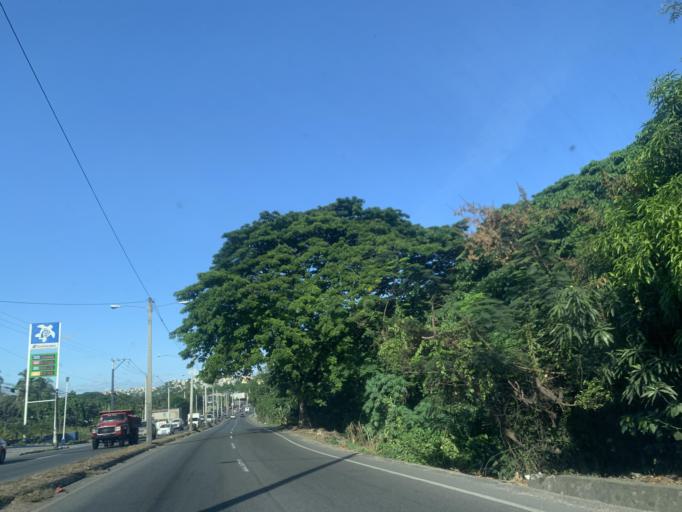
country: DO
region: San Cristobal
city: El Carril
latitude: 18.4355
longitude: -70.0184
